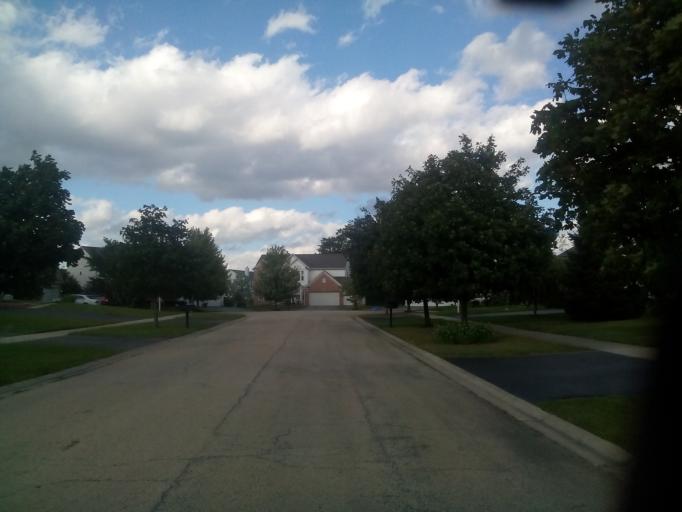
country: US
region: Illinois
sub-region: Will County
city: Bolingbrook
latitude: 41.7003
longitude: -88.1381
